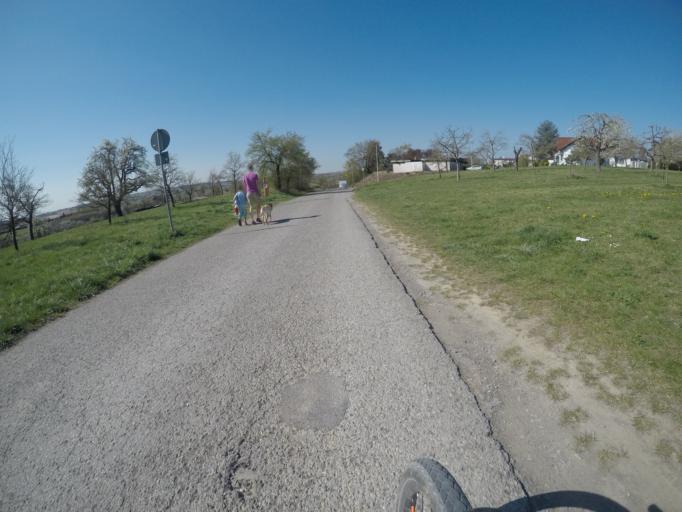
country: DE
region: Baden-Wuerttemberg
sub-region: Regierungsbezirk Stuttgart
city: Herrenberg
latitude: 48.5633
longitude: 8.9182
